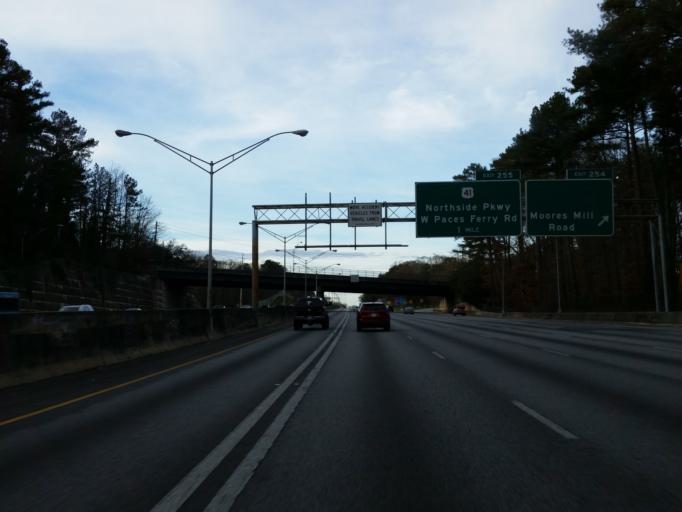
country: US
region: Georgia
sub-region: Cobb County
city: Vinings
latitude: 33.8302
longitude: -84.4257
